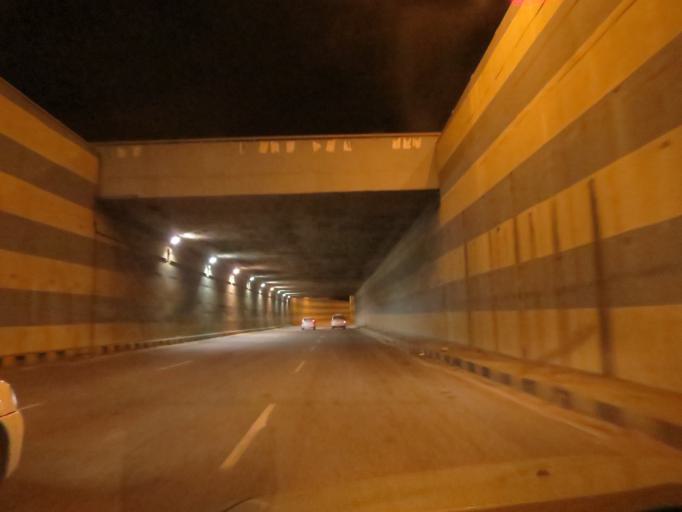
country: IN
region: Karnataka
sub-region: Bangalore Urban
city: Bangalore
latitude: 13.0275
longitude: 77.6332
